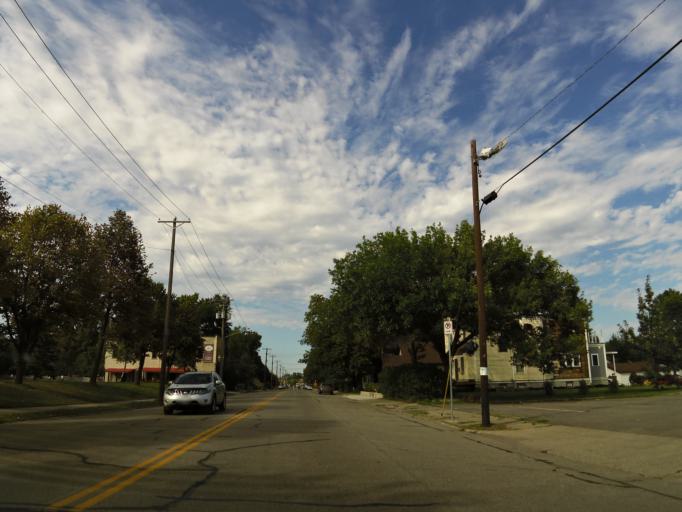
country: US
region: Minnesota
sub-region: Hennepin County
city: Minneapolis
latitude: 45.0088
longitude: -93.2717
